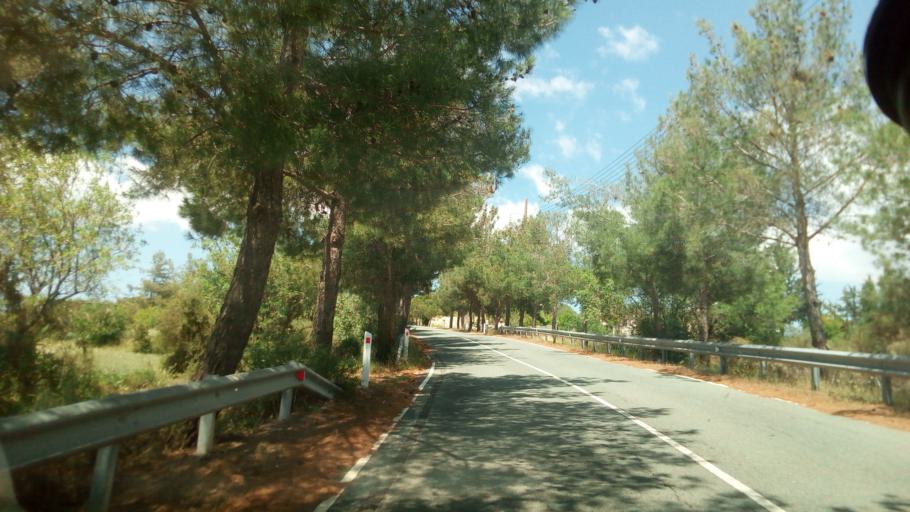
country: CY
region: Limassol
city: Pachna
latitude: 34.8320
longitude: 32.7723
